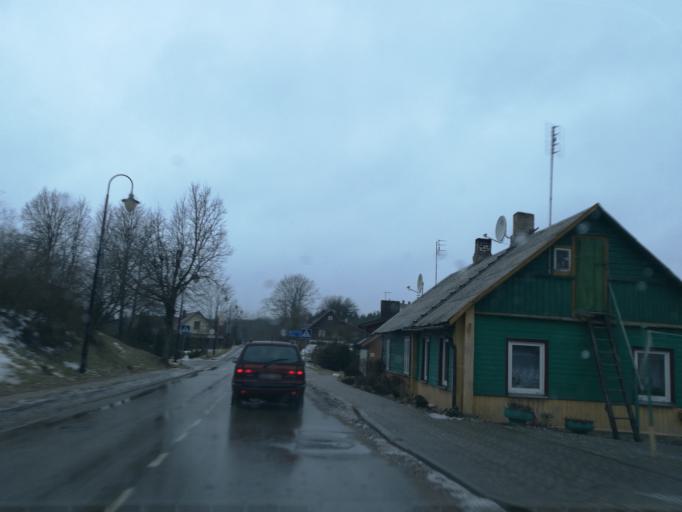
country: LT
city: Trakai
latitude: 54.6526
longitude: 24.9207
